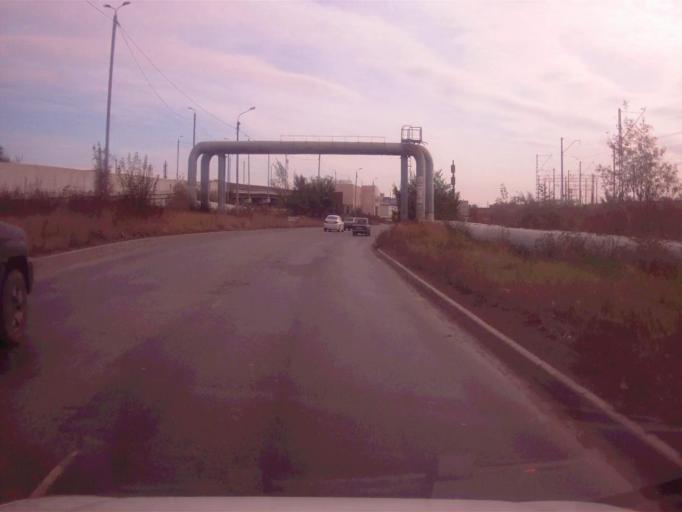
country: RU
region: Chelyabinsk
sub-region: Gorod Chelyabinsk
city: Chelyabinsk
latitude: 55.1584
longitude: 61.4387
